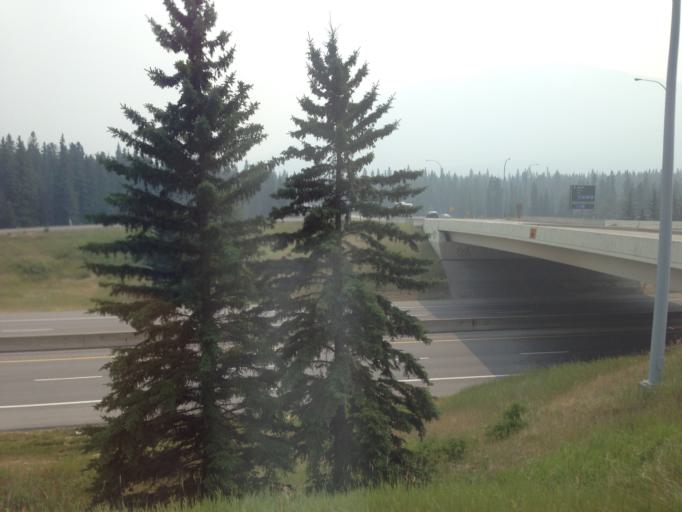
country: CA
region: Alberta
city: Banff
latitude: 51.1884
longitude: -115.5831
